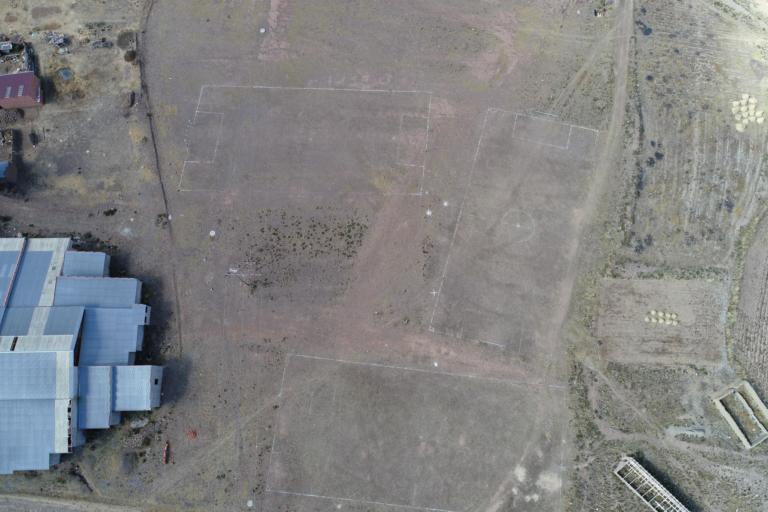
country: BO
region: La Paz
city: Achacachi
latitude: -15.8988
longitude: -68.9095
